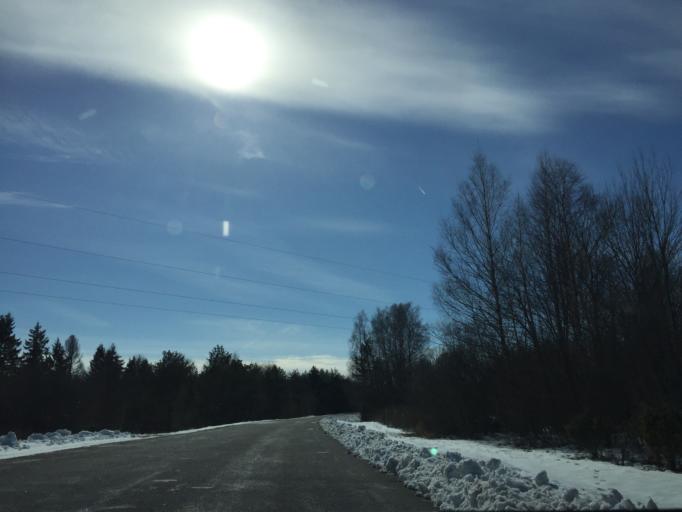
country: EE
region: Saare
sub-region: Orissaare vald
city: Orissaare
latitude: 58.4021
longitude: 22.9938
